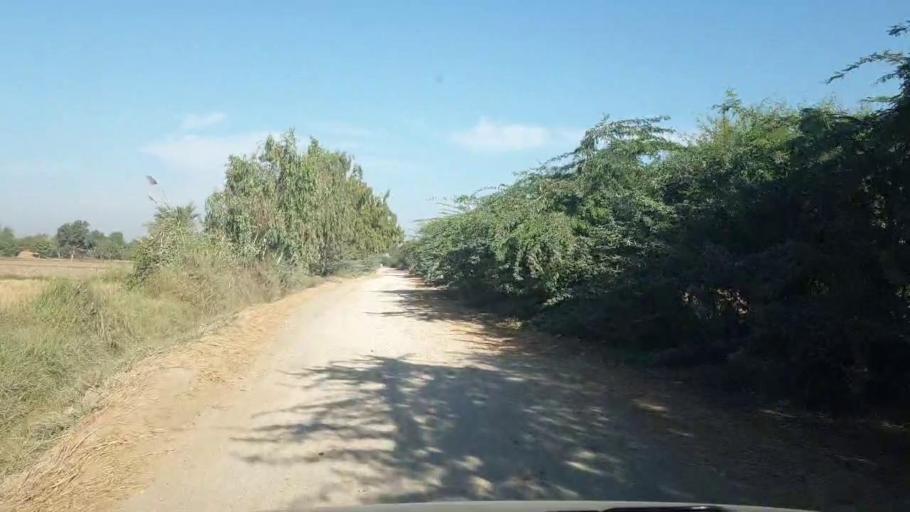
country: PK
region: Sindh
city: Talhar
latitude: 24.9074
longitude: 68.8096
